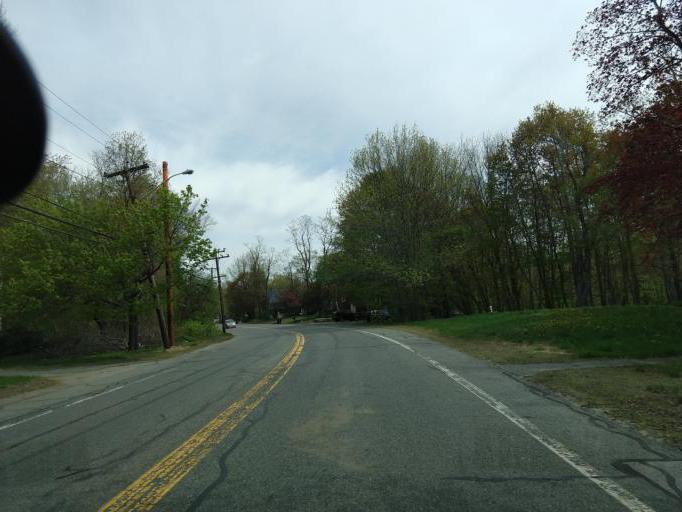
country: US
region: Massachusetts
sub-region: Essex County
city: Merrimac
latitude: 42.8146
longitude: -71.0271
